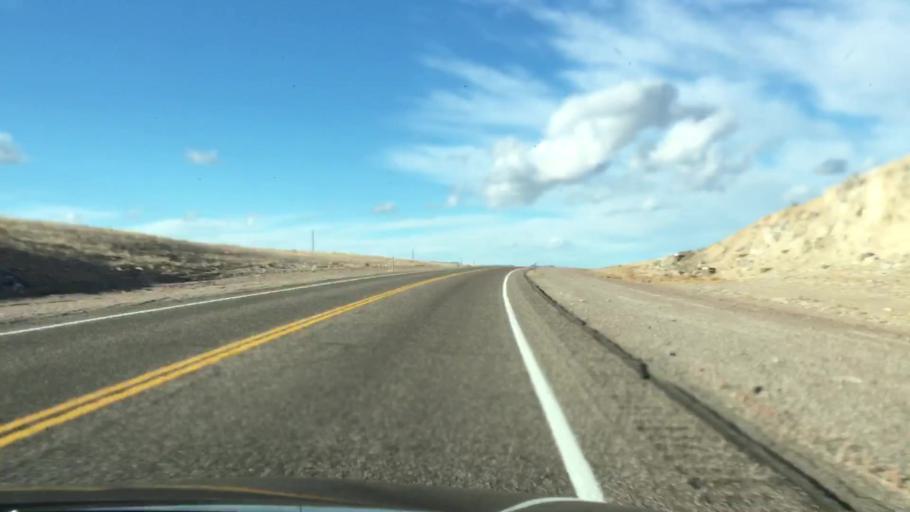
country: US
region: Nevada
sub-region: Esmeralda County
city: Goldfield
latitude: 37.3870
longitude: -117.1433
